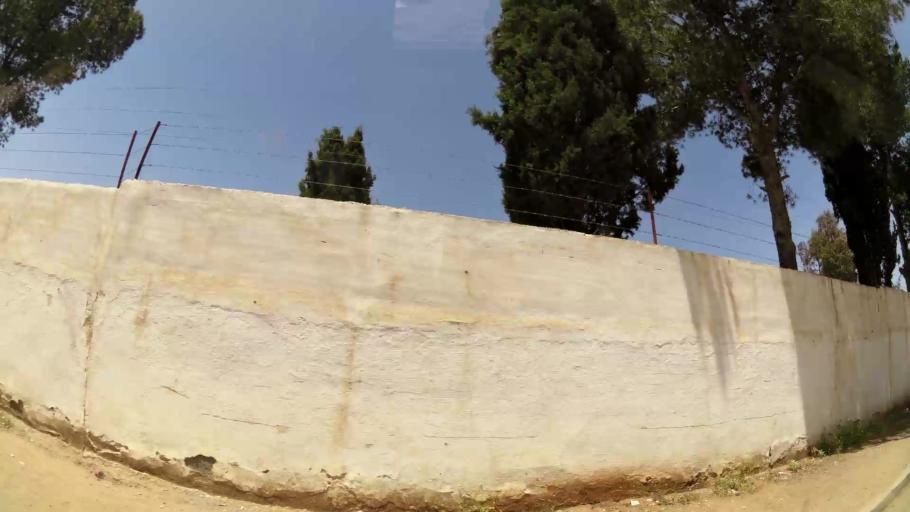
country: MA
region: Rabat-Sale-Zemmour-Zaer
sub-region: Khemisset
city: Khemisset
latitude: 33.8290
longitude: -6.0917
